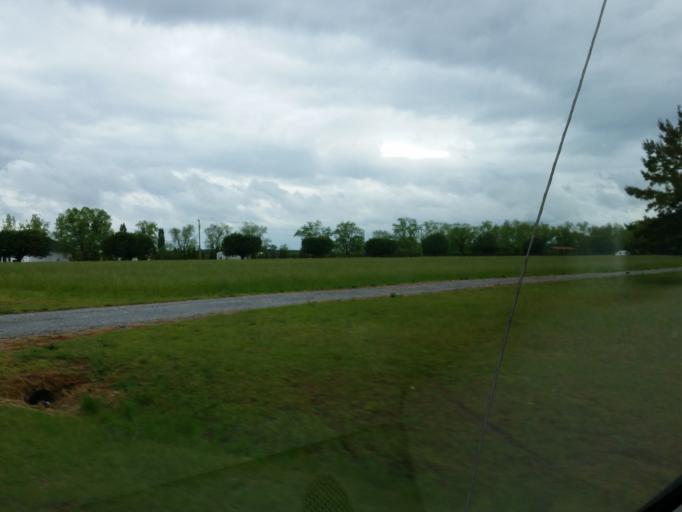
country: US
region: Georgia
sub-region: Peach County
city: Byron
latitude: 32.6768
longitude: -83.8390
